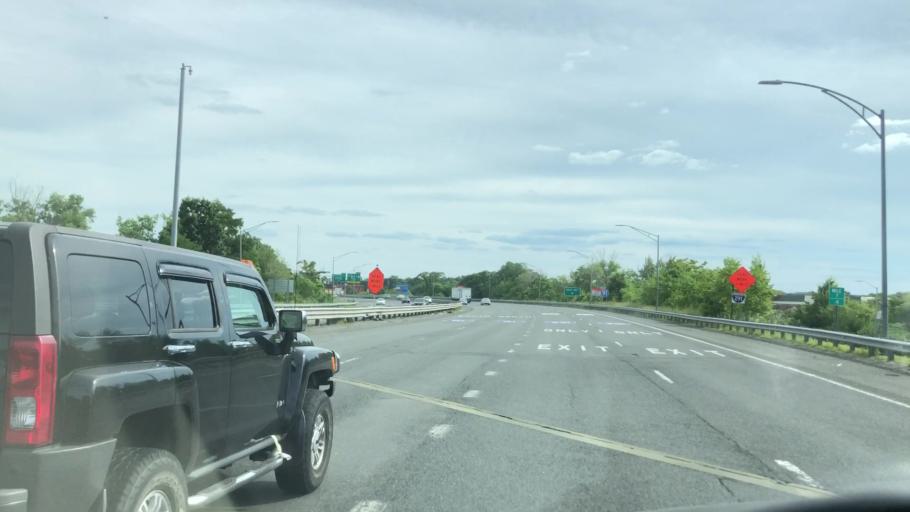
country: US
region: Massachusetts
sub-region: Hampden County
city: West Springfield
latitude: 42.1235
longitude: -72.6093
